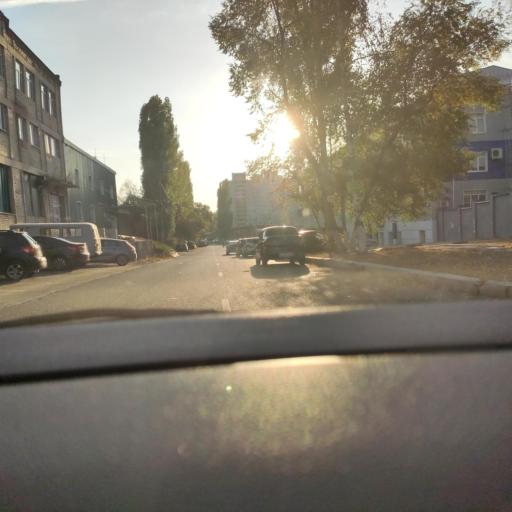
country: RU
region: Voronezj
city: Voronezh
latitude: 51.6595
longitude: 39.1413
